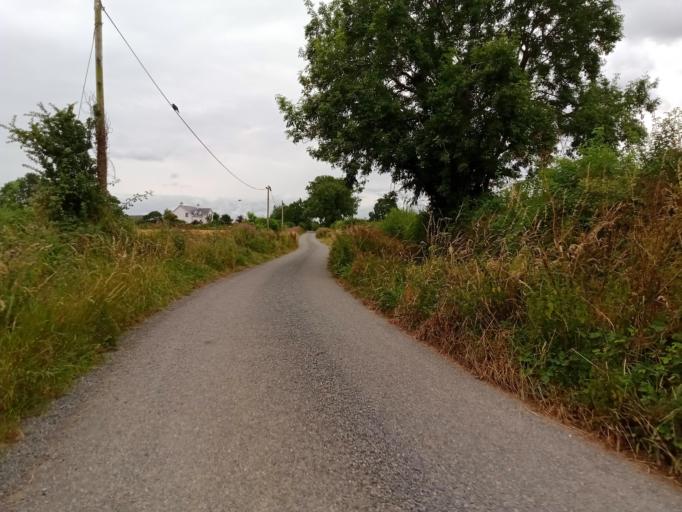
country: IE
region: Leinster
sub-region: Kilkenny
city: Callan
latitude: 52.5419
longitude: -7.4142
